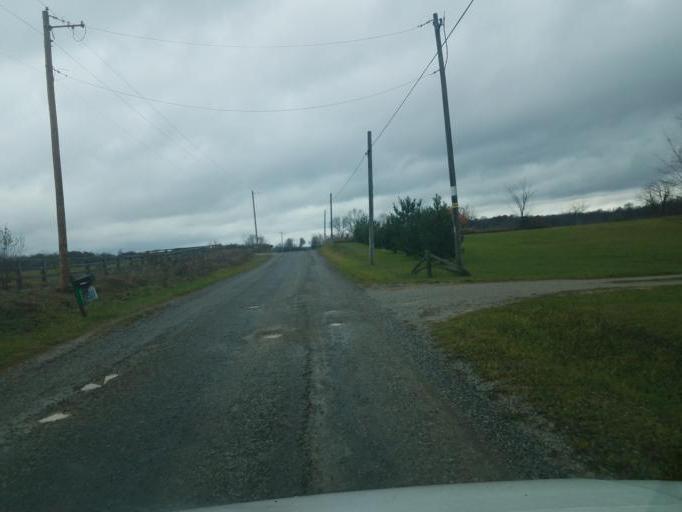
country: US
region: Ohio
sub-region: Morrow County
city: Mount Gilead
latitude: 40.5841
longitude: -82.7908
